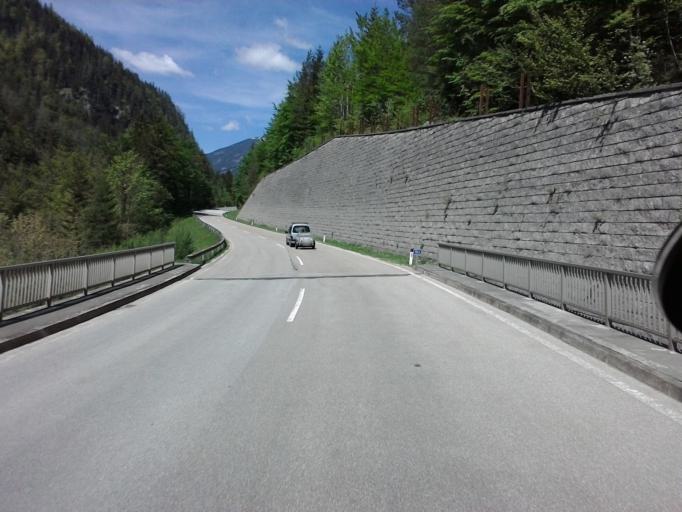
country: AT
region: Styria
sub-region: Politischer Bezirk Liezen
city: Palfau
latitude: 47.7046
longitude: 14.8609
